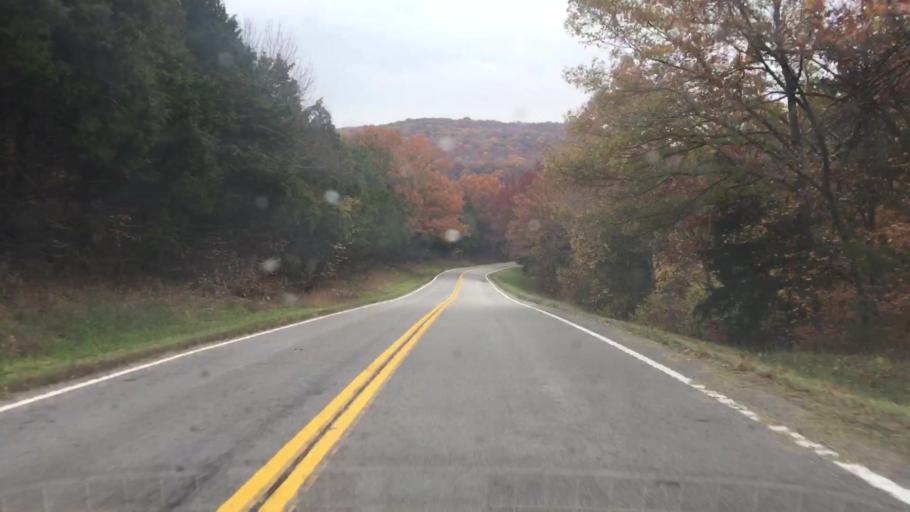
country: US
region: Missouri
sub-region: Gasconade County
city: Hermann
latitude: 38.7091
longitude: -91.6308
